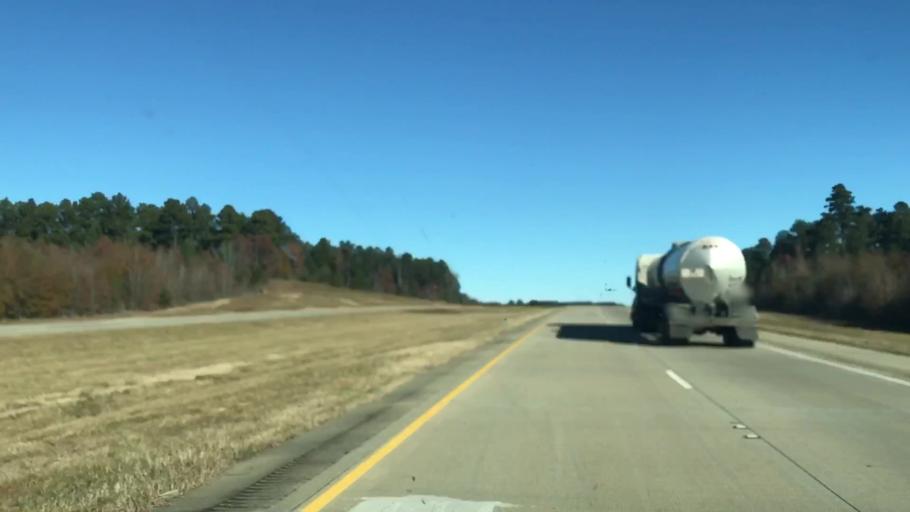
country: US
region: Louisiana
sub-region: Caddo Parish
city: Vivian
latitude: 32.9887
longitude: -93.9105
